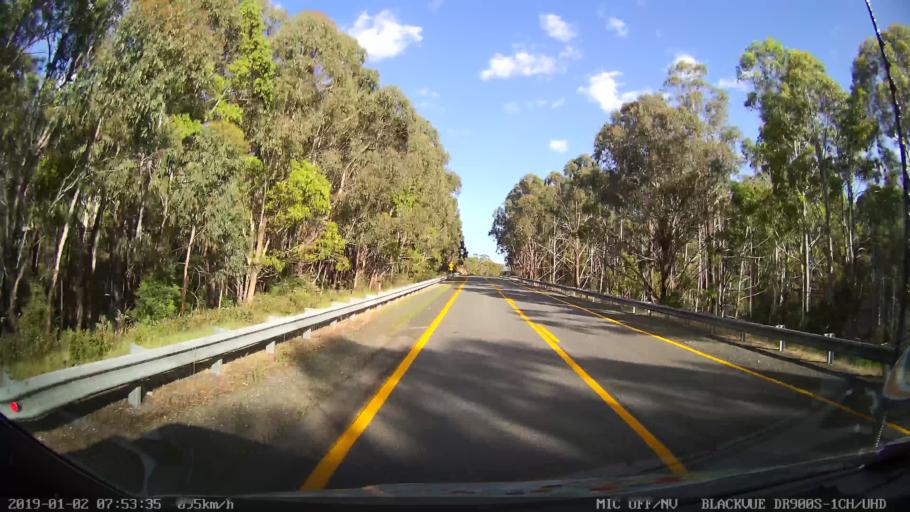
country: AU
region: New South Wales
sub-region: Tumut Shire
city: Tumut
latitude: -35.7035
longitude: 148.5044
